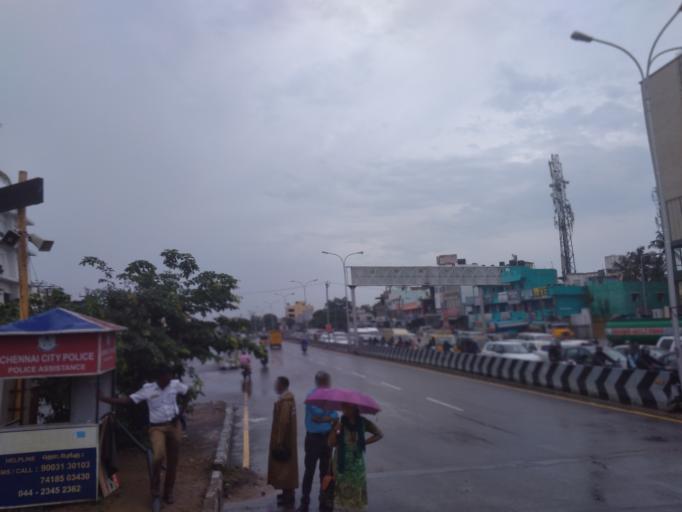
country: IN
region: Tamil Nadu
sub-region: Kancheepuram
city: Perungudi
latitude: 12.9489
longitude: 80.2406
